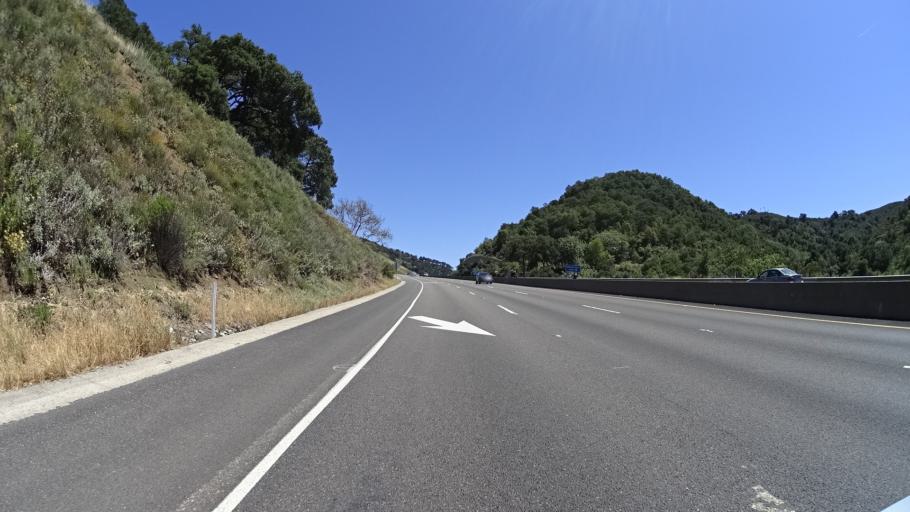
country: US
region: California
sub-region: San Luis Obispo County
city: Santa Margarita
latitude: 35.3511
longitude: -120.6331
